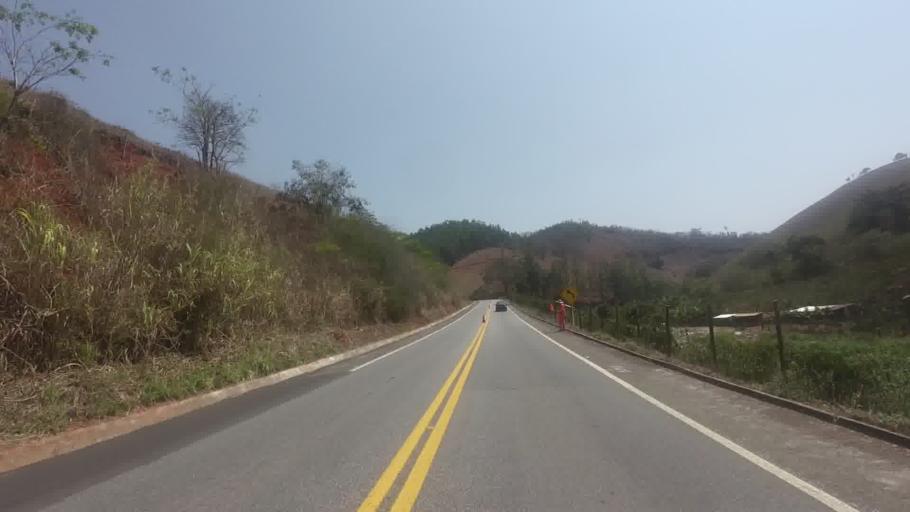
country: BR
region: Espirito Santo
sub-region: Mimoso Do Sul
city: Mimoso do Sul
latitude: -20.9232
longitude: -41.3135
